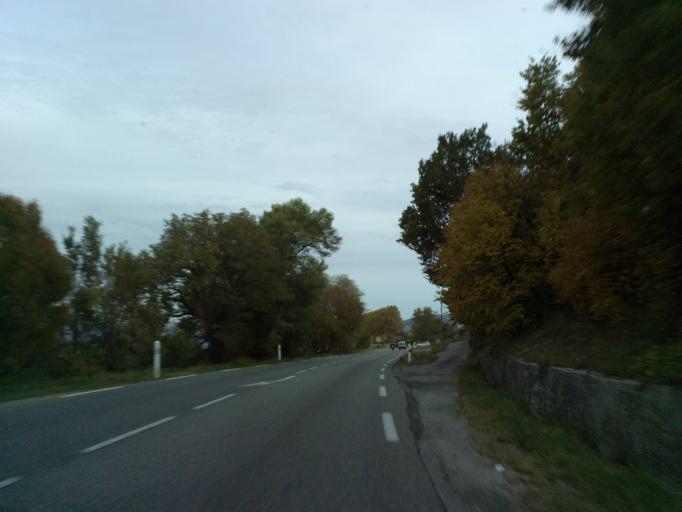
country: FR
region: Provence-Alpes-Cote d'Azur
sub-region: Departement des Alpes-de-Haute-Provence
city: Peipin
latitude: 44.1504
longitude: 5.9582
